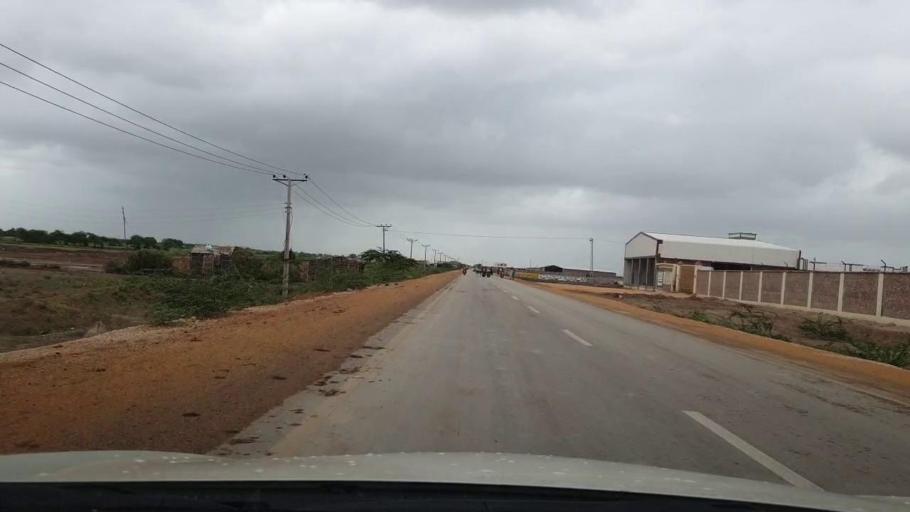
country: PK
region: Sindh
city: Badin
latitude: 24.6537
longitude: 68.7657
